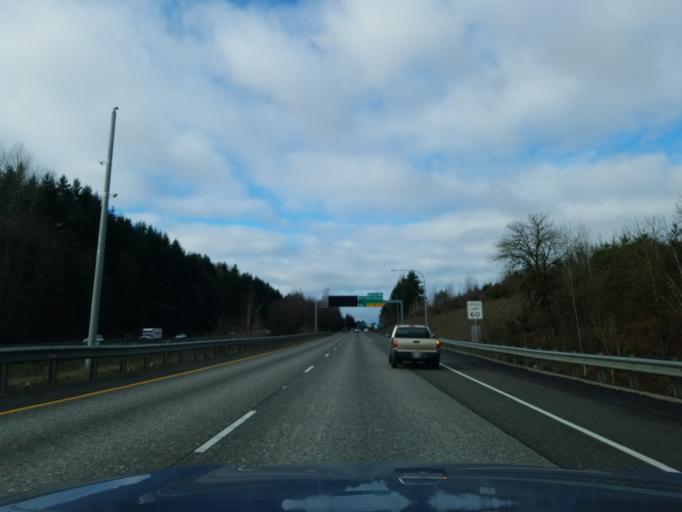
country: US
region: Washington
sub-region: Clark County
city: Salmon Creek
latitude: 45.7120
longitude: -122.6394
